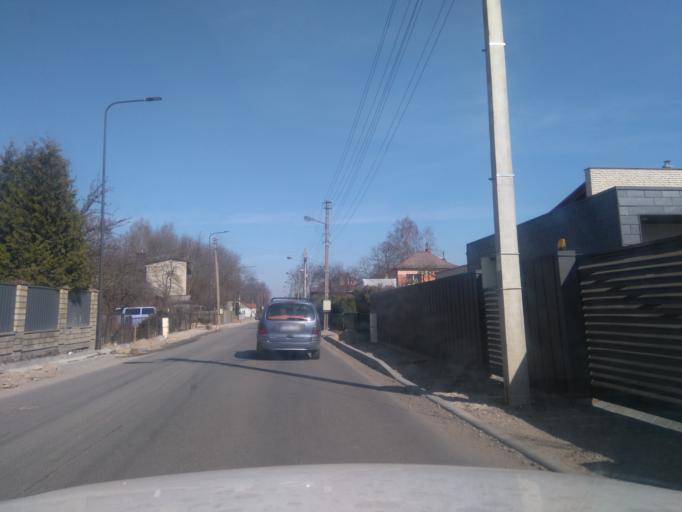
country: LT
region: Kauno apskritis
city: Dainava (Kaunas)
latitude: 54.8886
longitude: 23.9544
